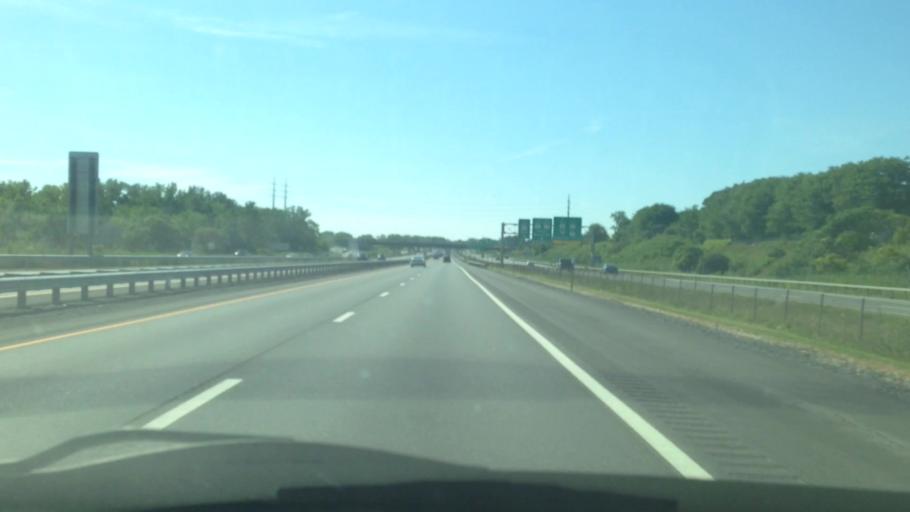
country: US
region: New York
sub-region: Oneida County
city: Utica
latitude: 43.1181
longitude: -75.2199
